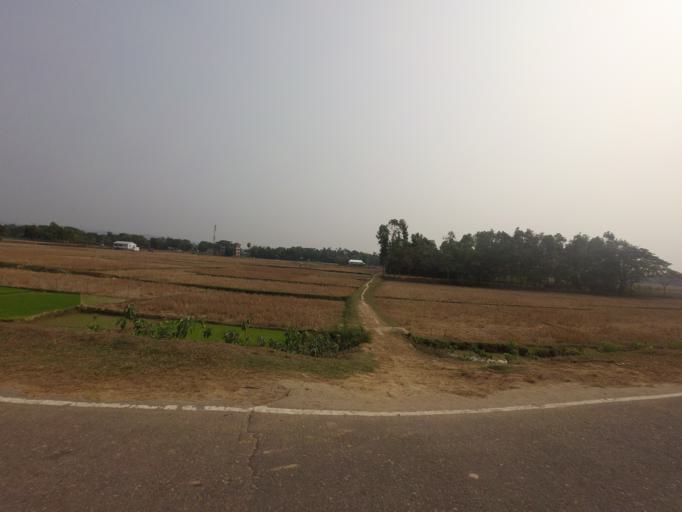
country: BD
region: Dhaka
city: Netrakona
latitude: 25.1545
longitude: 90.6590
